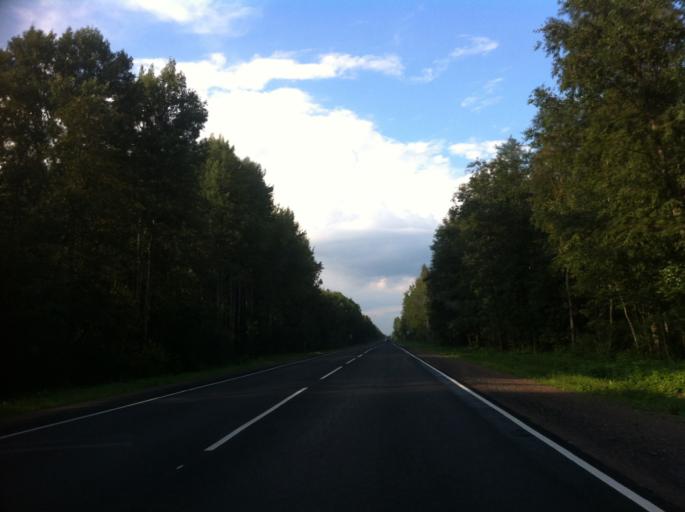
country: RU
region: Leningrad
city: Luga
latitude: 58.4914
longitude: 29.7819
